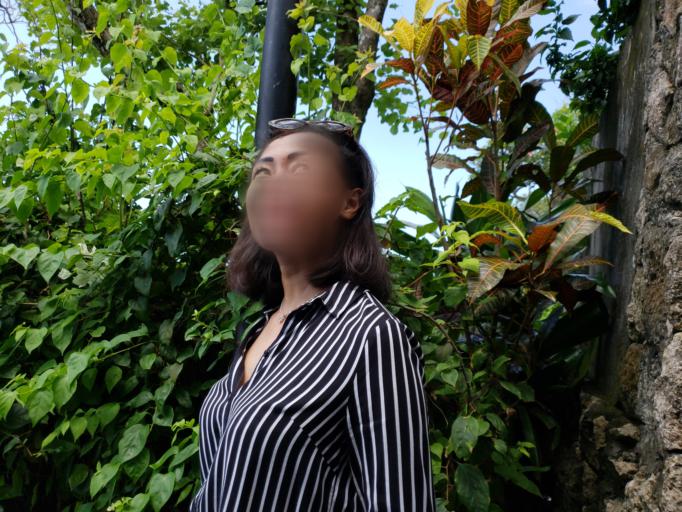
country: ID
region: Bali
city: Pecatu
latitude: -8.8451
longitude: 115.1194
